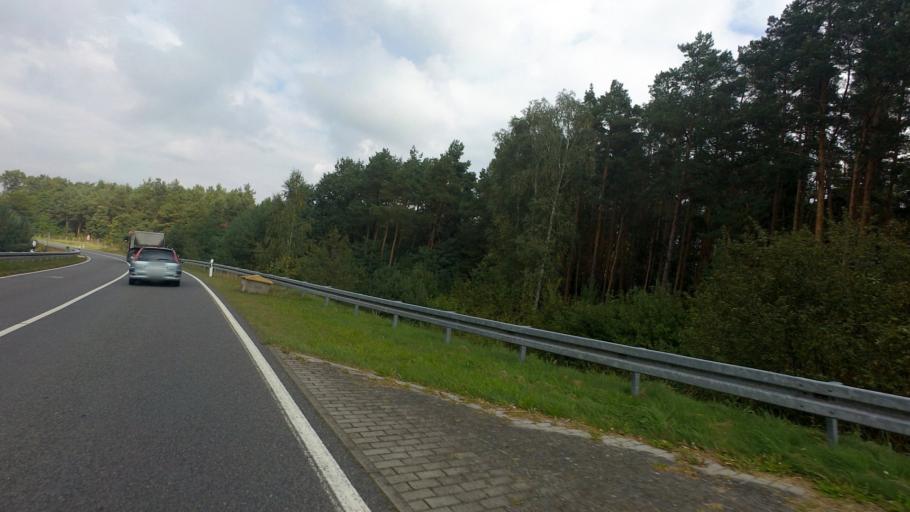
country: DE
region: Brandenburg
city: Bad Liebenwerda
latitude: 51.5315
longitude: 13.4110
